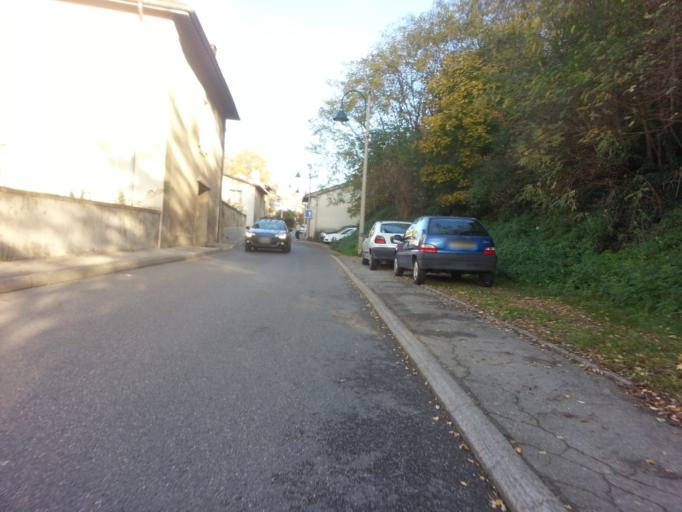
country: FR
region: Rhone-Alpes
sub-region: Departement de la Drome
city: Chabeuil
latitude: 44.9028
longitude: 5.0228
